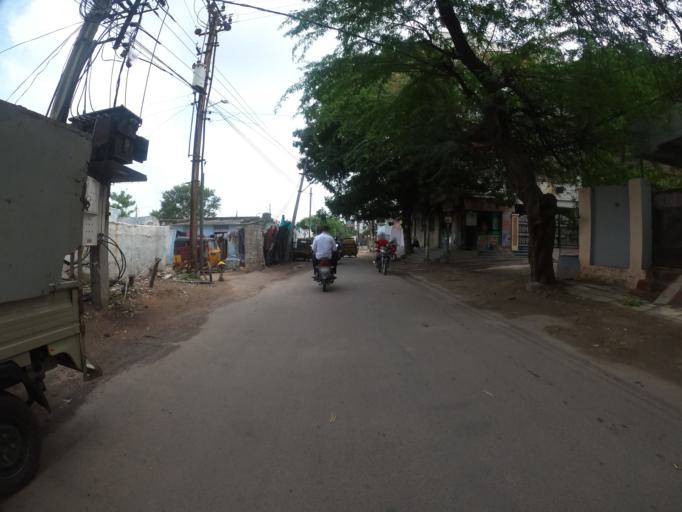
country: IN
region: Telangana
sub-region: Hyderabad
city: Hyderabad
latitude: 17.3934
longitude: 78.4174
